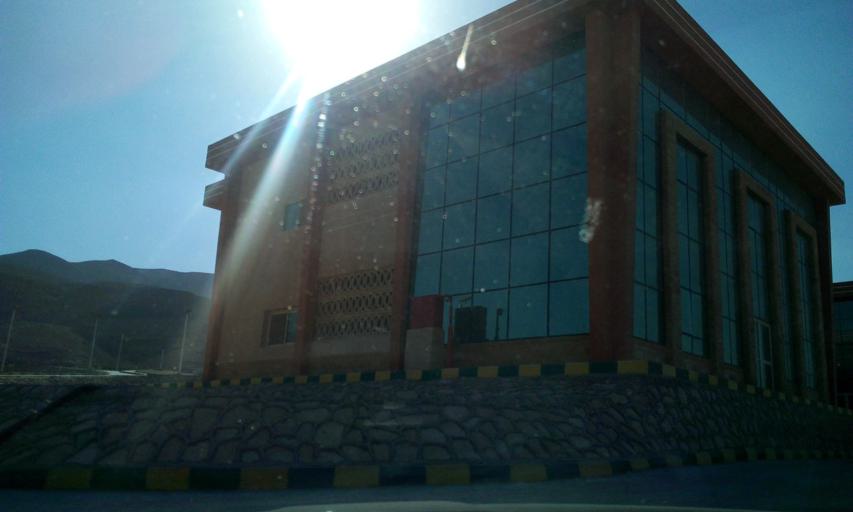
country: EG
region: As Suways
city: Ain Sukhna
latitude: 29.4273
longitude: 32.3797
